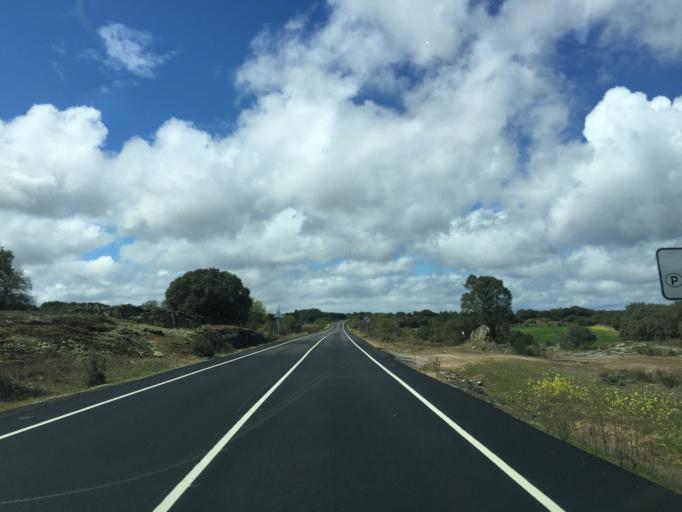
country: ES
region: Castille and Leon
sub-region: Provincia de Zamora
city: Moralina
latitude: 41.4804
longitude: -6.1393
